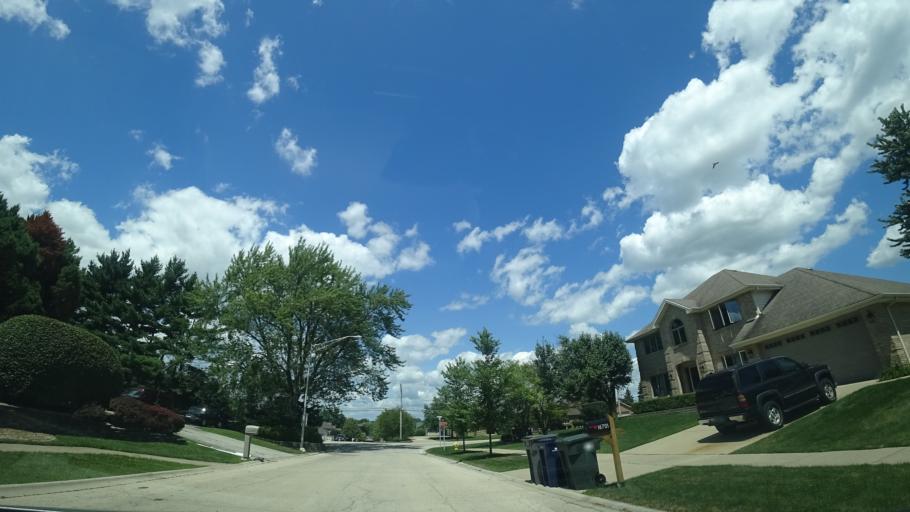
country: US
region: Illinois
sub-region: Cook County
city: Orland Hills
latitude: 41.5856
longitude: -87.8885
